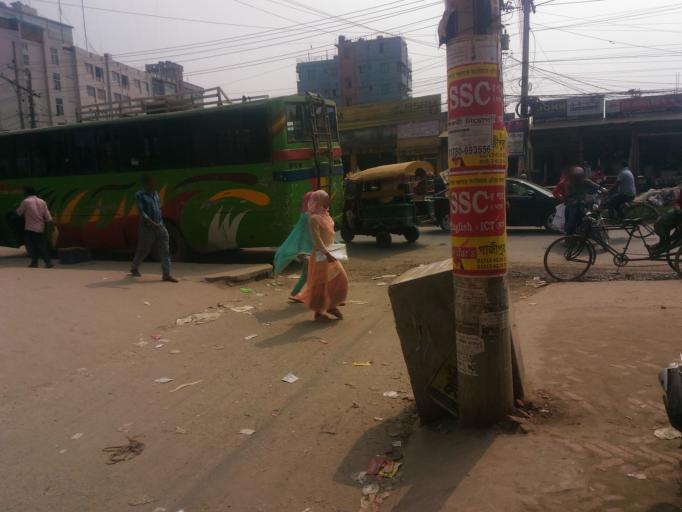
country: BD
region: Dhaka
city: Tungi
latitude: 23.9898
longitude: 90.3784
